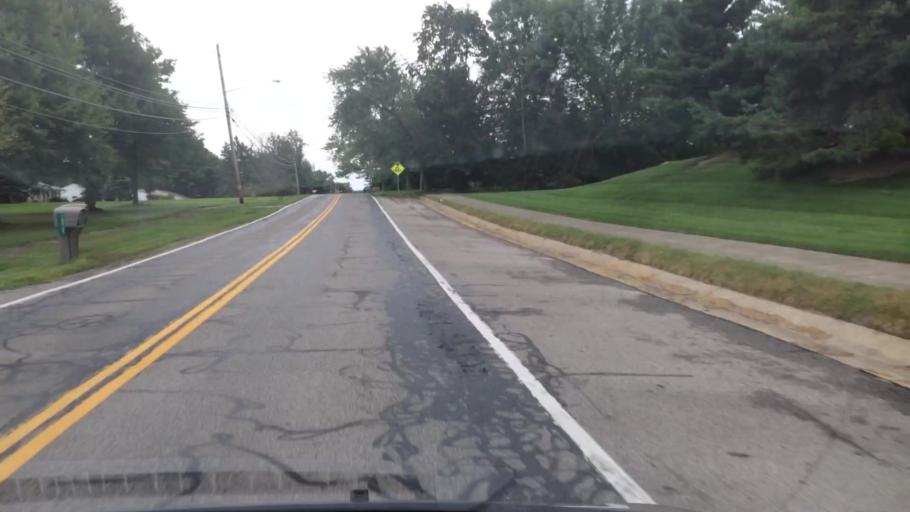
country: US
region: Ohio
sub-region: Cuyahoga County
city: Strongsville
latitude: 41.2826
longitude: -81.8110
